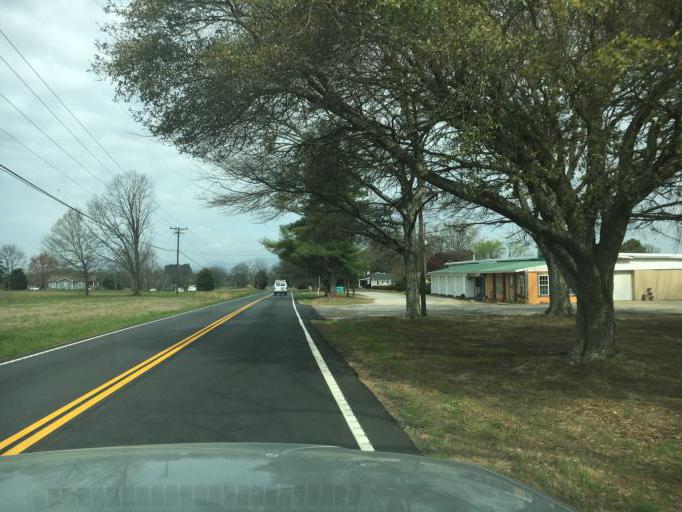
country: US
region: South Carolina
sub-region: Spartanburg County
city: Inman Mills
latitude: 35.0534
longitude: -82.1429
